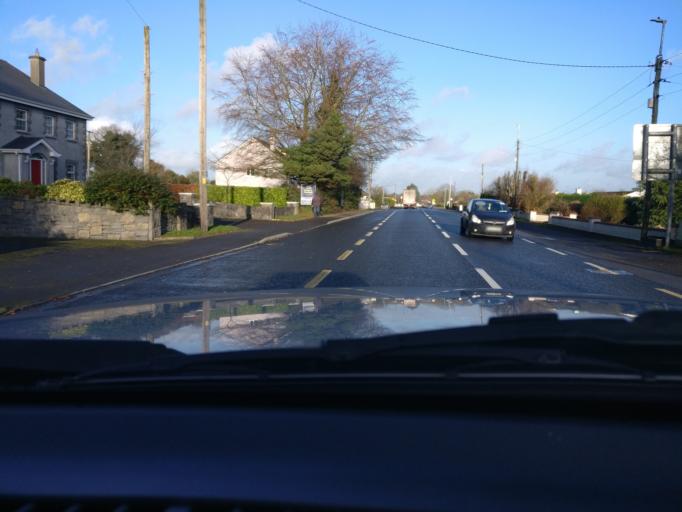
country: IE
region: Leinster
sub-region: An Iarmhi
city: Rathwire
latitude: 53.6149
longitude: -7.0902
